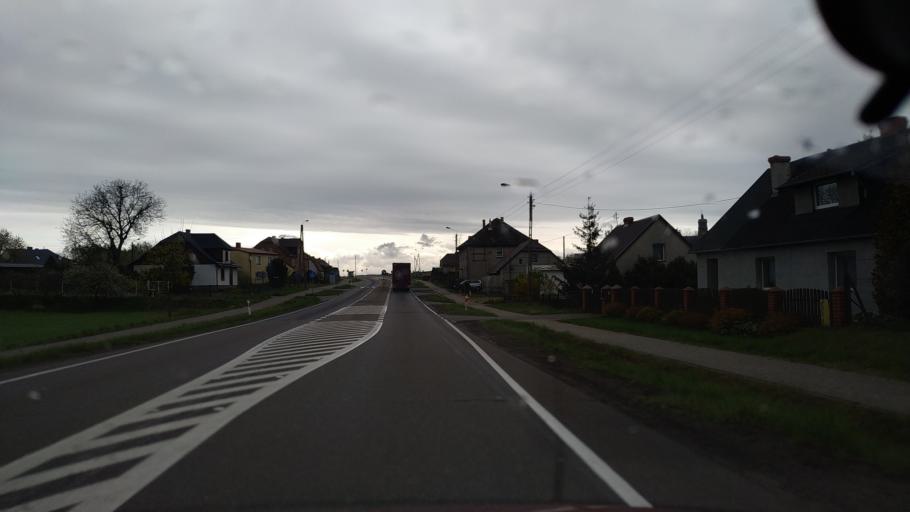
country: PL
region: Pomeranian Voivodeship
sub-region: Powiat starogardzki
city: Kaliska
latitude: 53.8872
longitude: 18.2126
